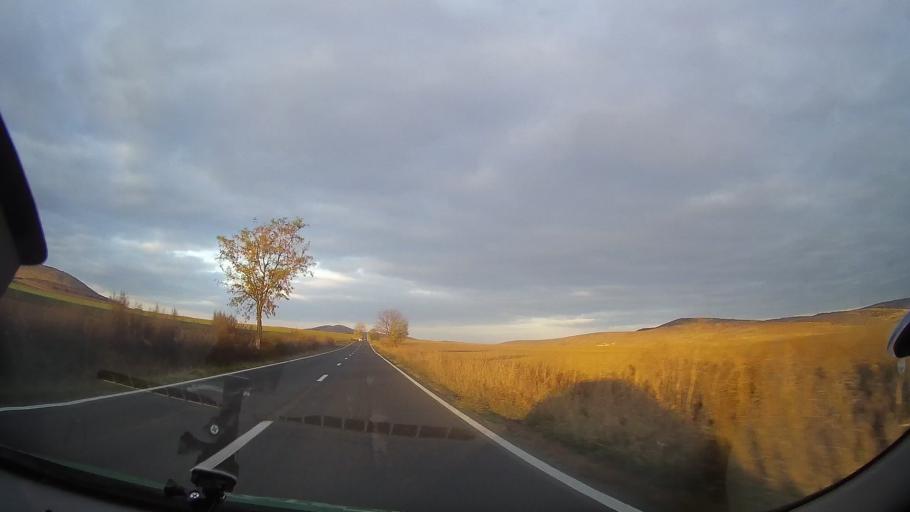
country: RO
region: Tulcea
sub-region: Comuna Nalbant
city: Nicolae Balcescu
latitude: 44.9733
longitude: 28.5419
